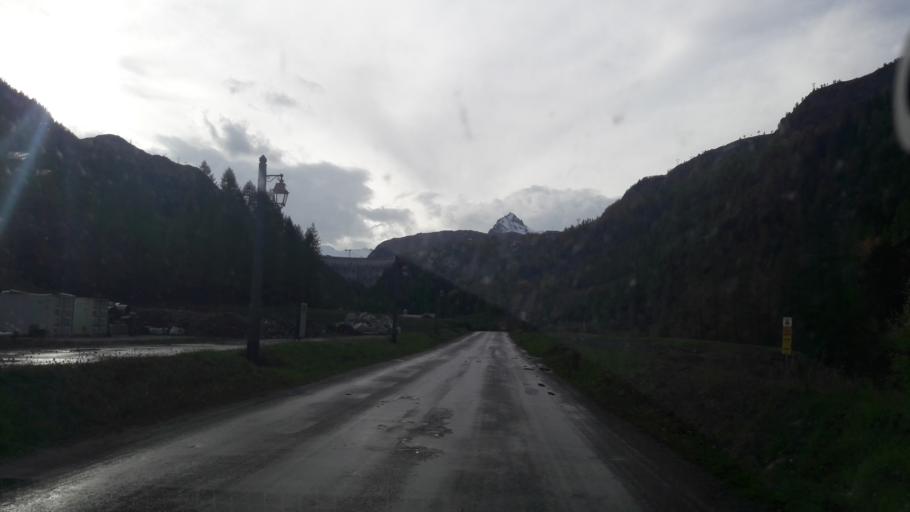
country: FR
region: Rhone-Alpes
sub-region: Departement de la Savoie
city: Tignes
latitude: 45.5136
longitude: 6.9157
